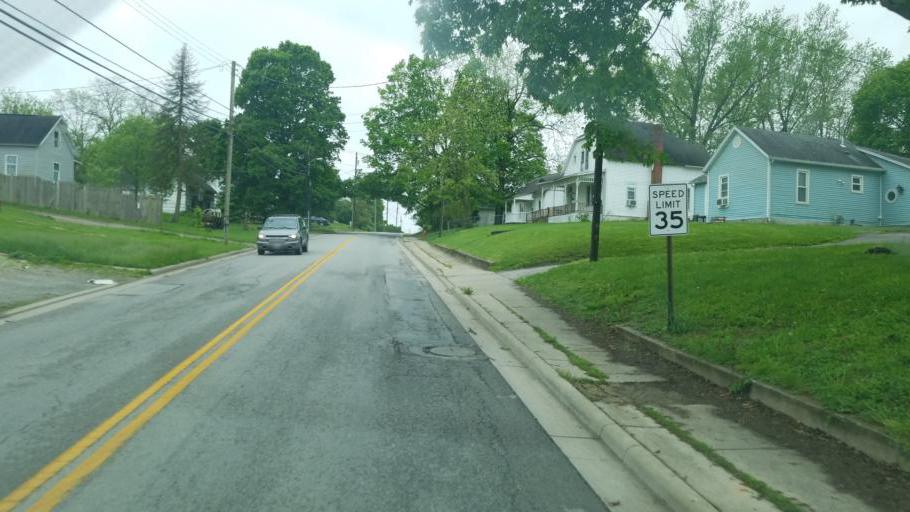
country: US
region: Ohio
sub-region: Highland County
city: Hillsboro
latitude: 39.2114
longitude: -83.6119
